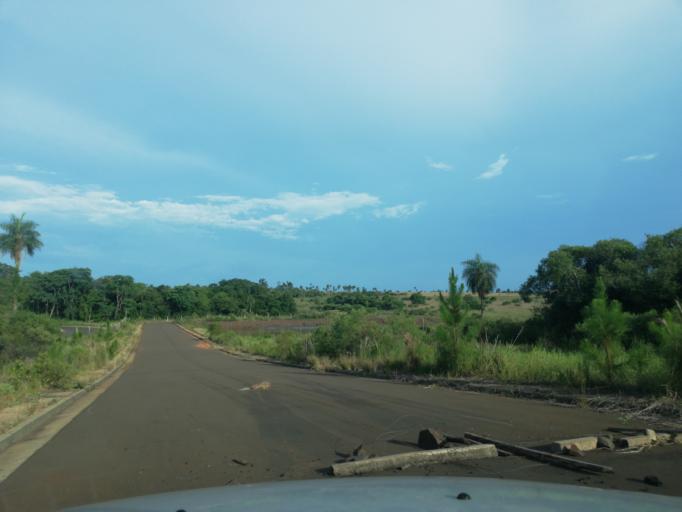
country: AR
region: Misiones
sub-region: Departamento de Candelaria
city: Candelaria
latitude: -27.4531
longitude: -55.7752
